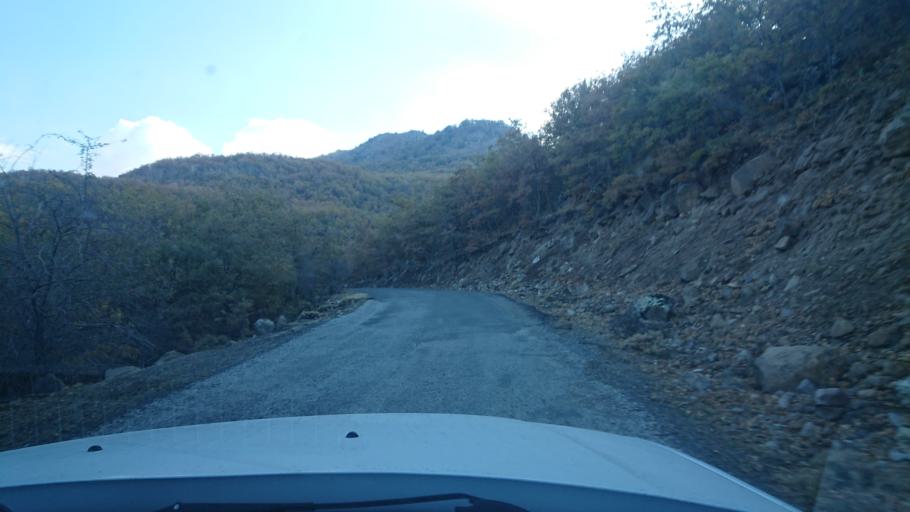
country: TR
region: Aksaray
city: Taspinar
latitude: 38.1699
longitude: 34.1899
